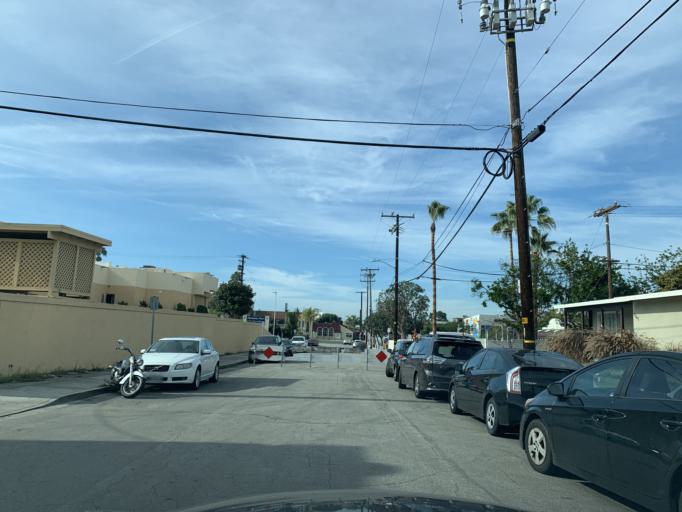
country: US
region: California
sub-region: Los Angeles County
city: Hermosa Beach
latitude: 33.8742
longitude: -118.3944
